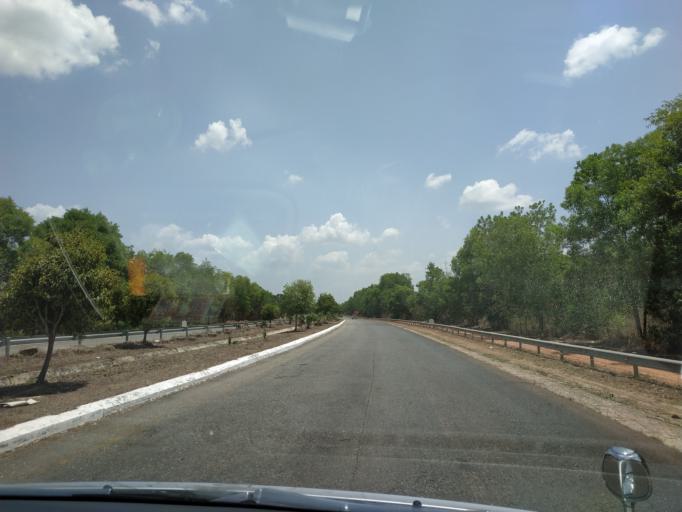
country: MM
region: Bago
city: Thanatpin
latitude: 17.1663
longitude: 96.1978
